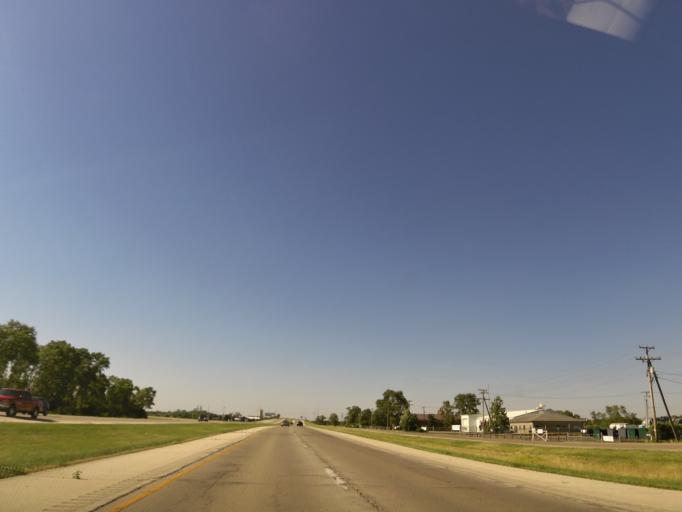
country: US
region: Illinois
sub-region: Winnebago County
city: Roscoe
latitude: 42.4500
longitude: -89.0198
